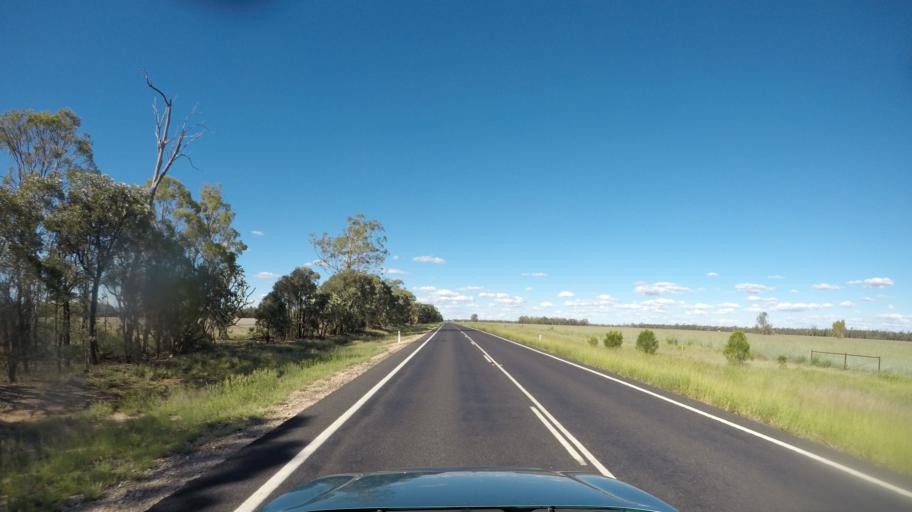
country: AU
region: Queensland
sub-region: Goondiwindi
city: Goondiwindi
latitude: -28.1361
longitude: 150.6955
